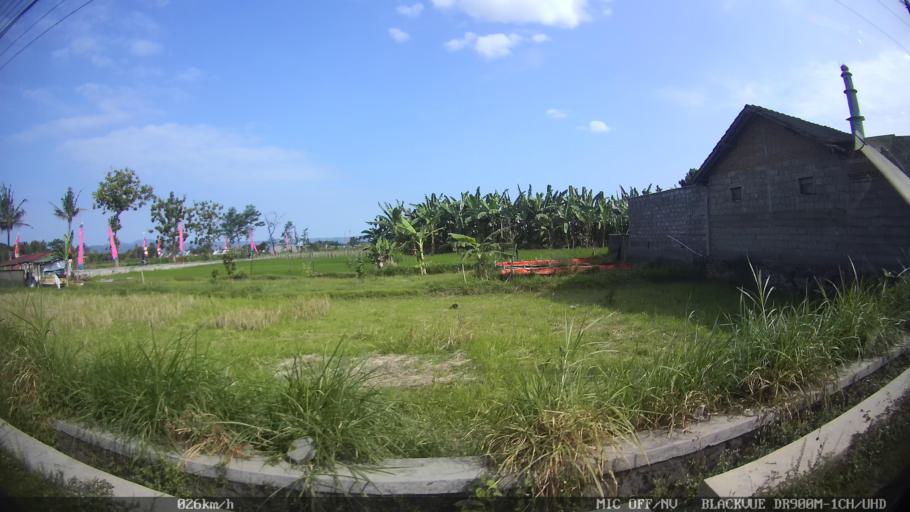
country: ID
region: Daerah Istimewa Yogyakarta
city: Depok
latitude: -7.7371
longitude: 110.4470
